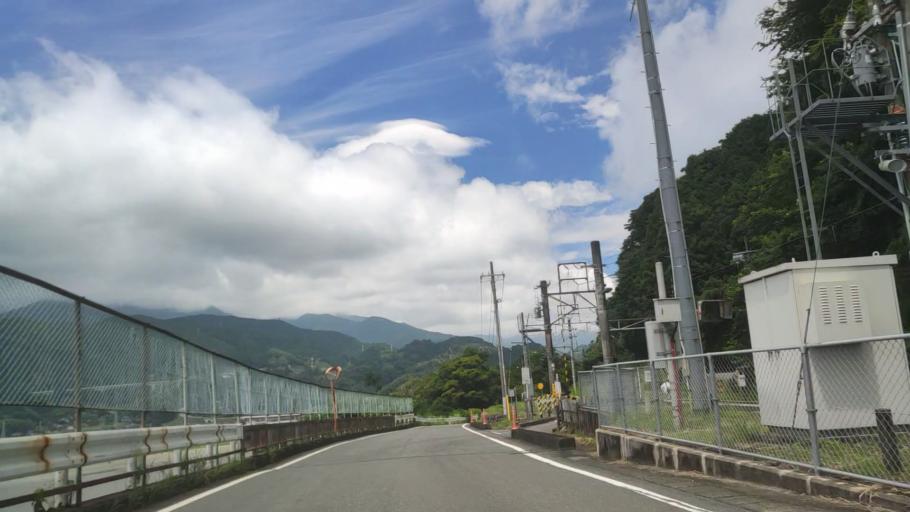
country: JP
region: Shizuoka
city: Fujinomiya
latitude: 35.2475
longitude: 138.4905
